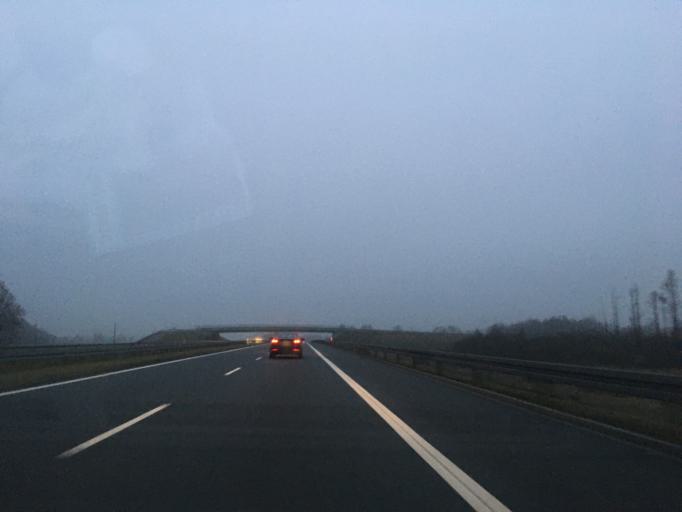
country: PL
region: Warmian-Masurian Voivodeship
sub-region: Powiat elblaski
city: Paslek
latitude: 54.0084
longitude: 19.6811
